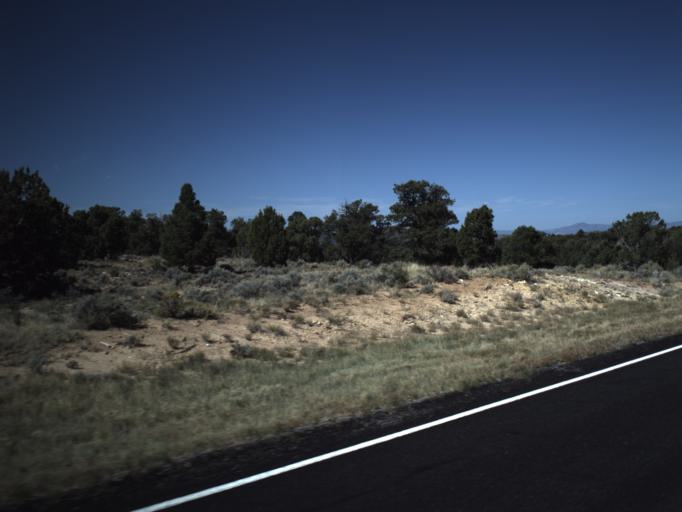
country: US
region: Utah
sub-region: Washington County
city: Enterprise
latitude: 37.6245
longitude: -113.4193
